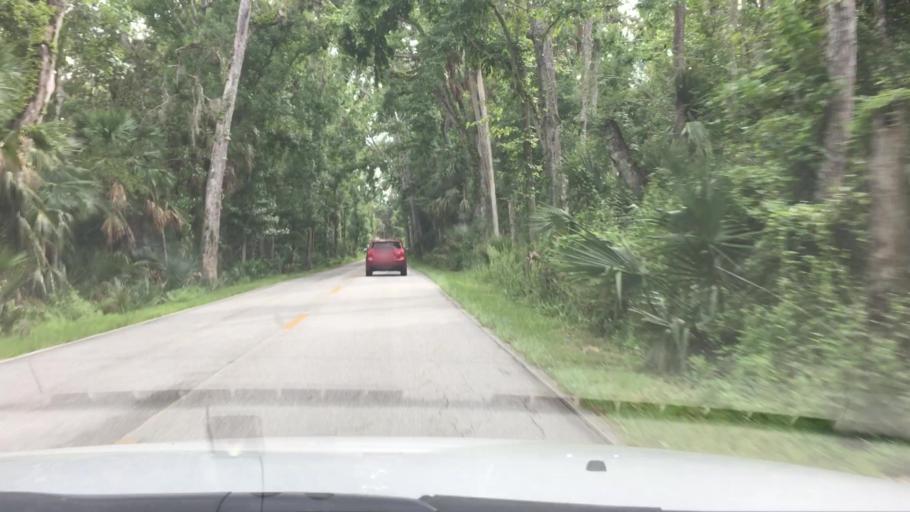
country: US
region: Florida
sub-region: Volusia County
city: Ormond-by-the-Sea
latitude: 29.3387
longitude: -81.1043
